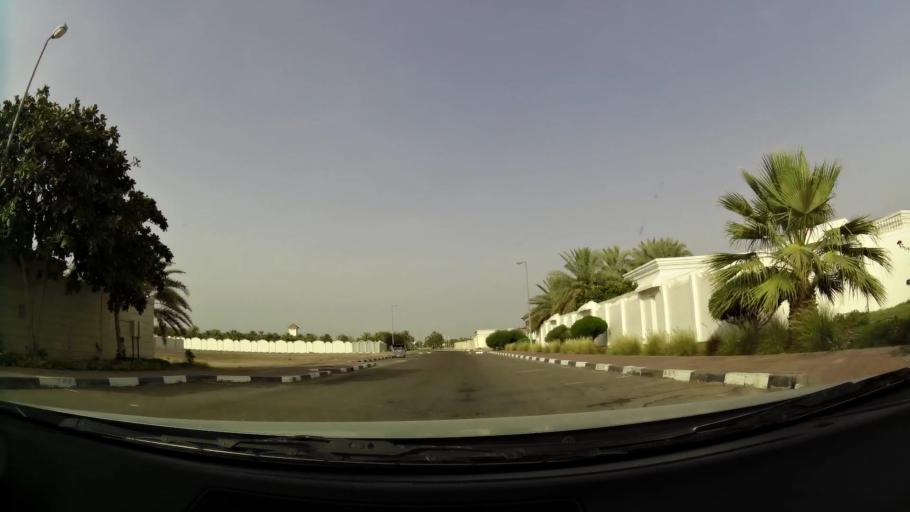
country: AE
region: Abu Dhabi
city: Al Ain
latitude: 24.2191
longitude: 55.6774
